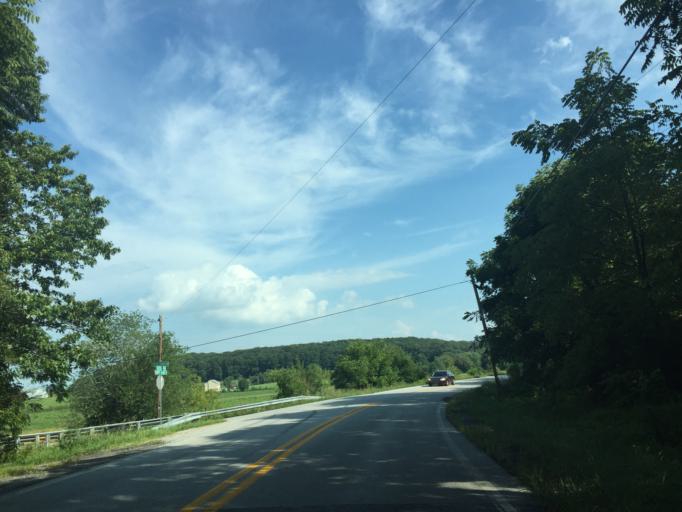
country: US
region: Maryland
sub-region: Carroll County
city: Manchester
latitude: 39.6275
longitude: -76.8925
